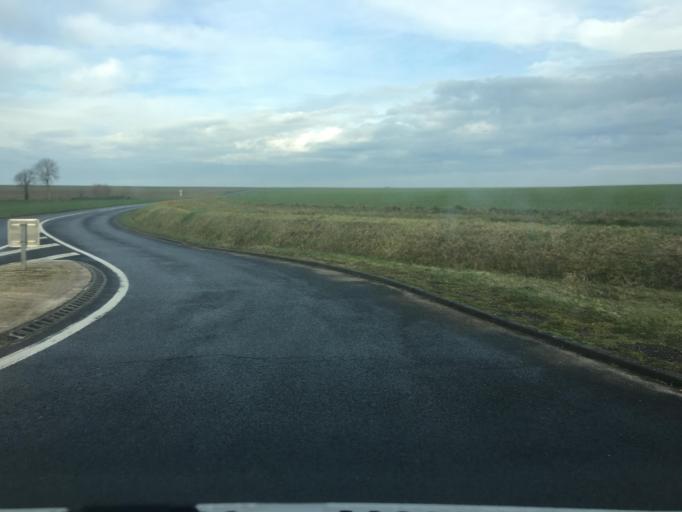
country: FR
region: Lower Normandy
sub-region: Departement du Calvados
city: Creully
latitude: 49.2934
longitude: -0.5433
